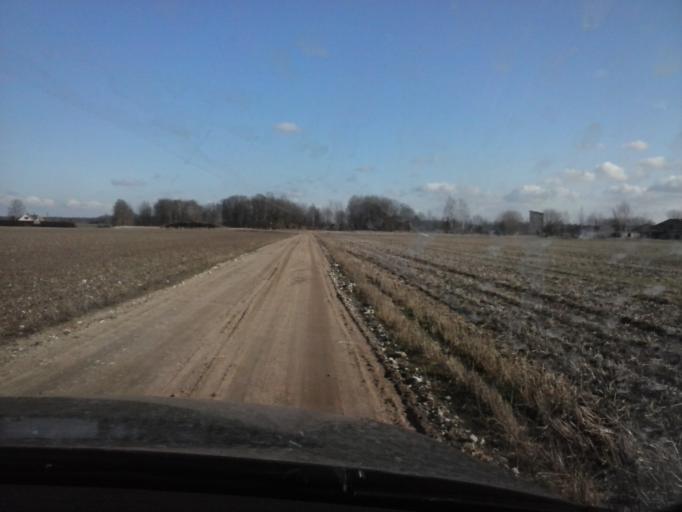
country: EE
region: Tartu
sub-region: Puhja vald
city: Puhja
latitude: 58.2848
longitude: 26.1575
